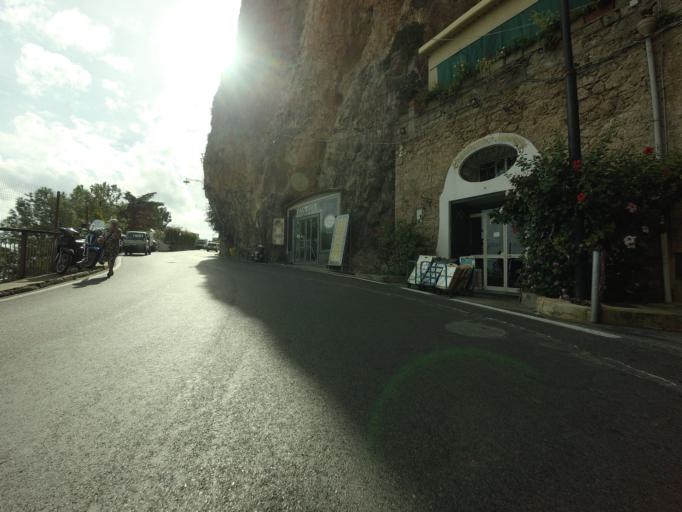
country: IT
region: Campania
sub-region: Provincia di Salerno
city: Positano
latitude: 40.6282
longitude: 14.4920
